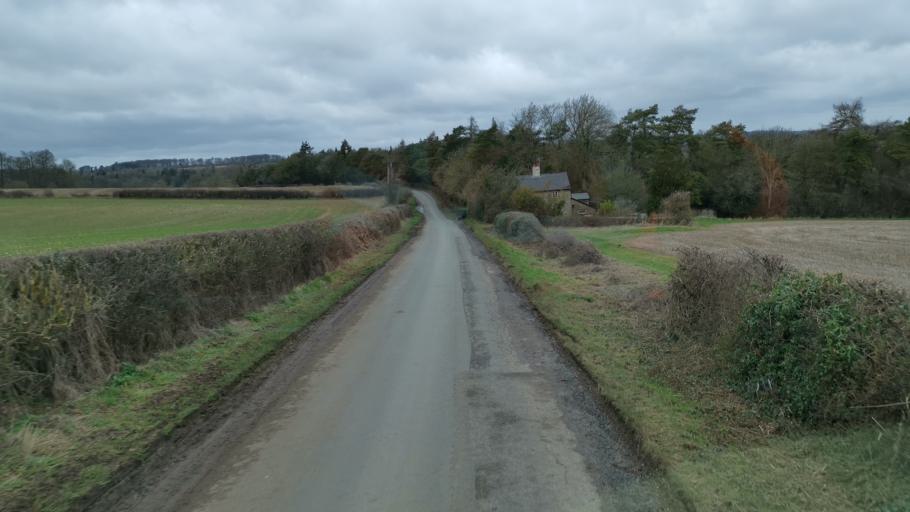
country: GB
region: England
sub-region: Oxfordshire
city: Somerton
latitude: 51.8985
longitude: -1.3082
